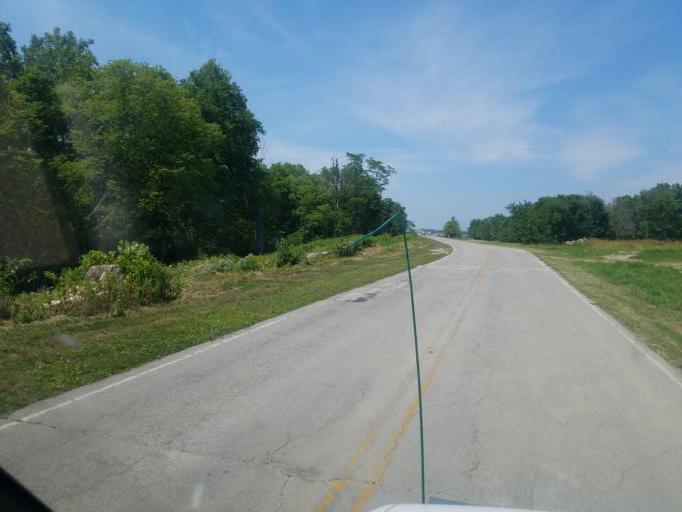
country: US
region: Ohio
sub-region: Mercer County
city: Celina
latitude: 40.5250
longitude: -84.5750
